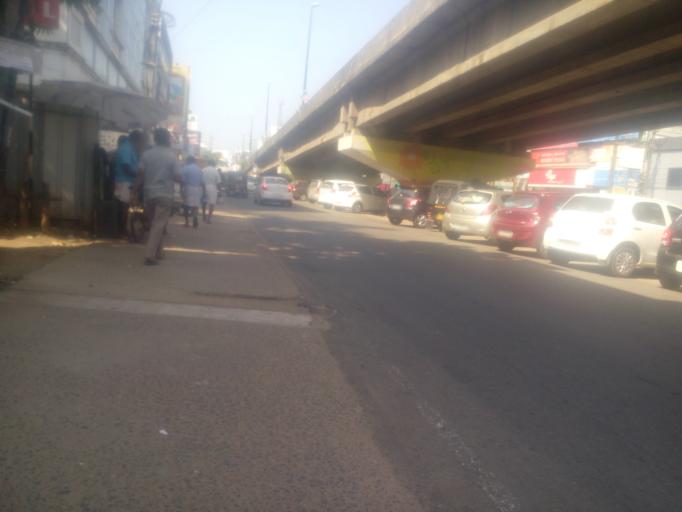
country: IN
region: Kerala
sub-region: Kozhikode
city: Kozhikode
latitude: 11.2590
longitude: 75.7907
